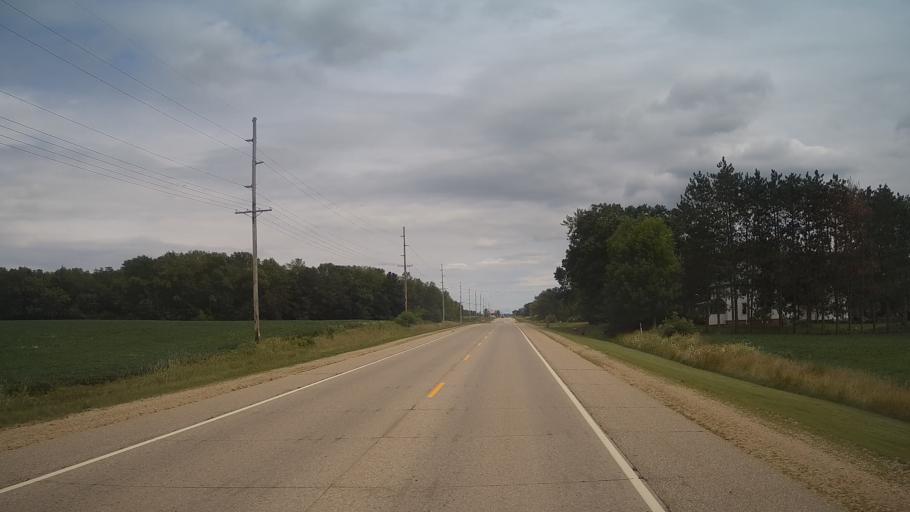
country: US
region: Wisconsin
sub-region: Green Lake County
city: Berlin
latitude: 44.0410
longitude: -89.0010
